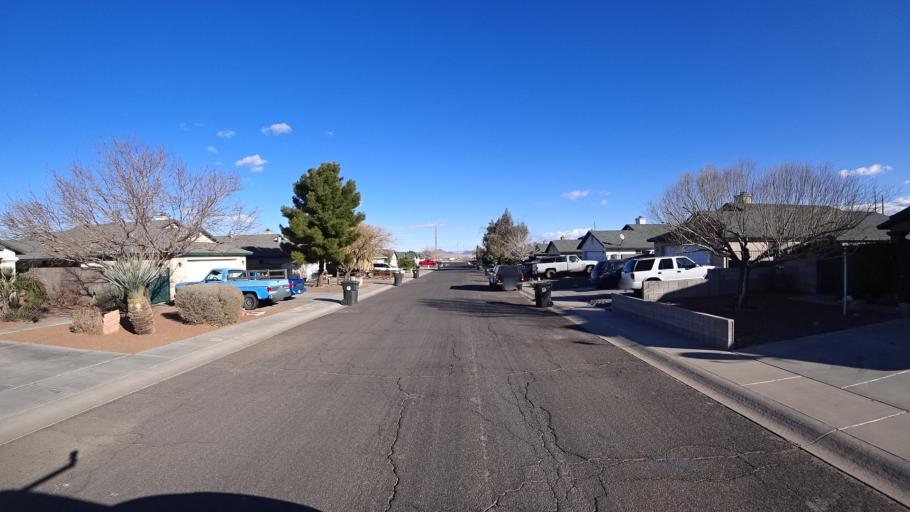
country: US
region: Arizona
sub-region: Mohave County
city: New Kingman-Butler
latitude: 35.2232
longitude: -113.9951
